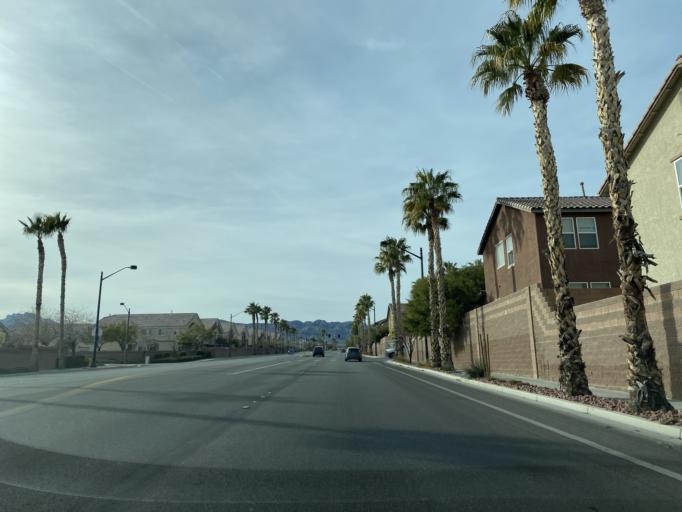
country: US
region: Nevada
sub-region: Clark County
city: Summerlin South
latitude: 36.2919
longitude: -115.2927
